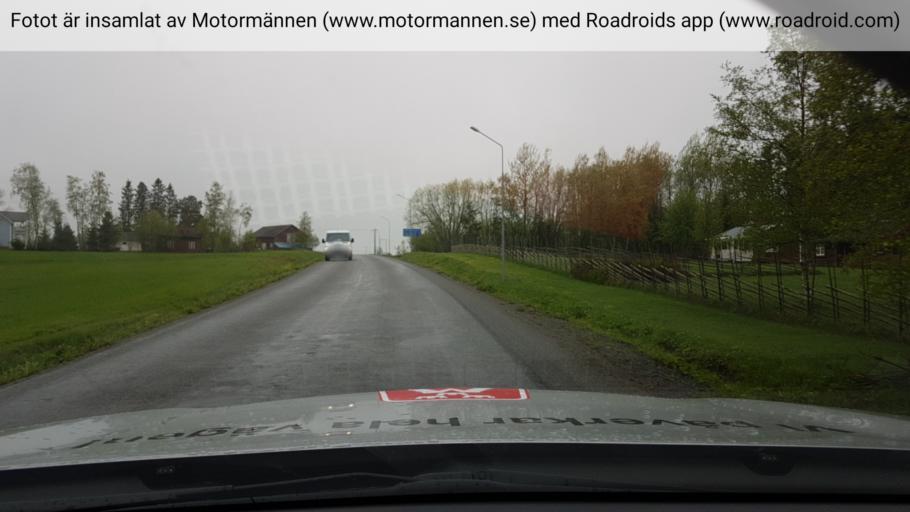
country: SE
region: Jaemtland
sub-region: Bergs Kommun
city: Hoverberg
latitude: 62.9968
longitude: 14.3251
